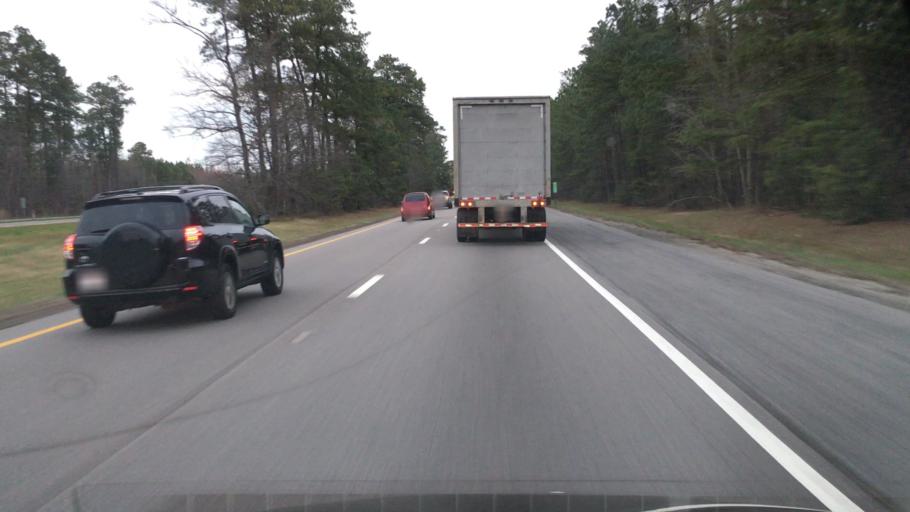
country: US
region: Virginia
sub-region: City of Emporia
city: Emporia
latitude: 36.8377
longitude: -77.4432
